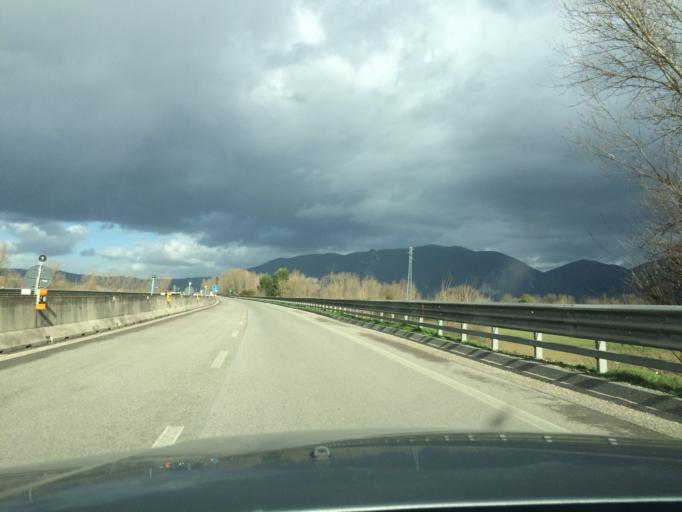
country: IT
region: Umbria
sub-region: Provincia di Terni
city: Terni
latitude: 42.5542
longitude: 12.5839
